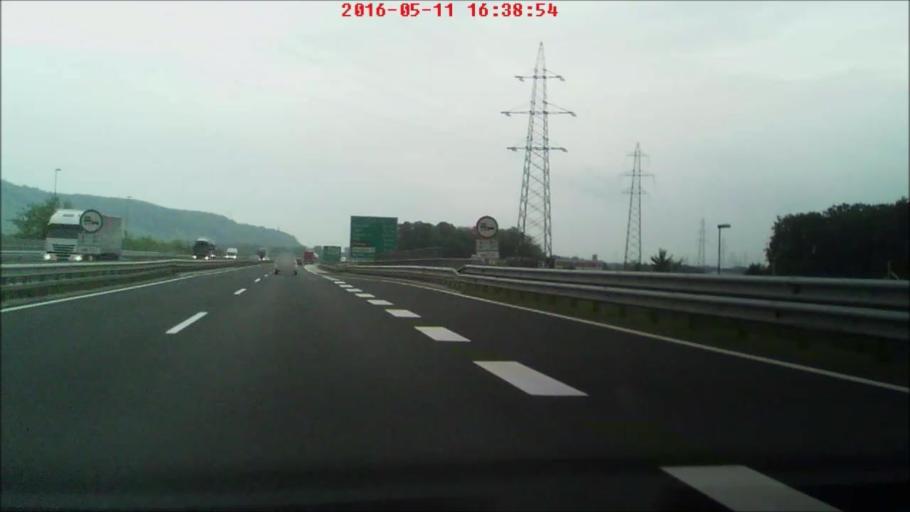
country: SI
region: Miklavz na Dravskem Polju
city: Miklavz na Dravskem Polju
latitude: 46.5449
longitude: 15.6951
